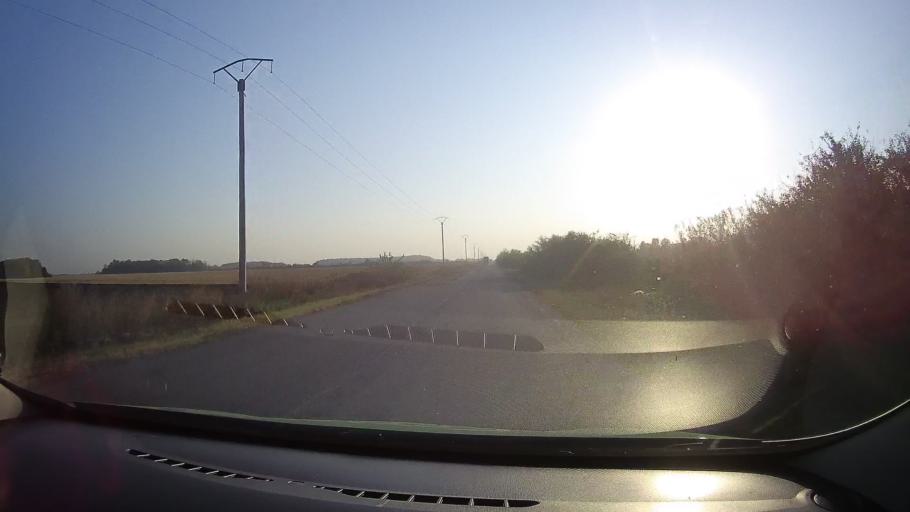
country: RO
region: Arad
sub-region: Comuna Zimandu Nou
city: Andrei Saguna
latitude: 46.3576
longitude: 21.3864
